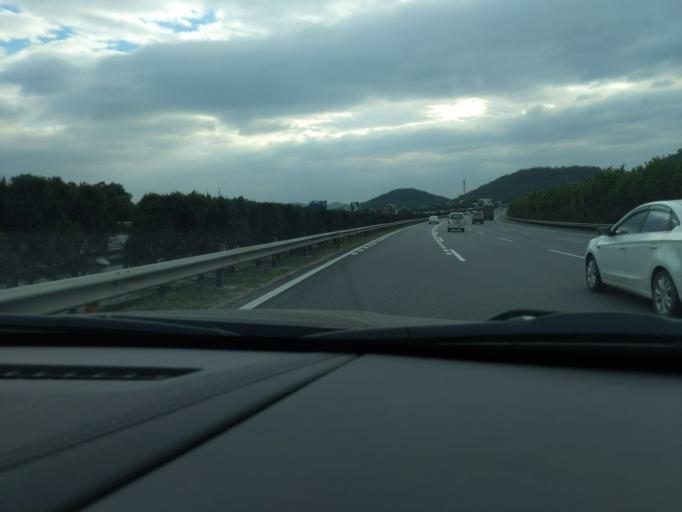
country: CN
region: Fujian
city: Maxiang
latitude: 24.6857
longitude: 118.3228
